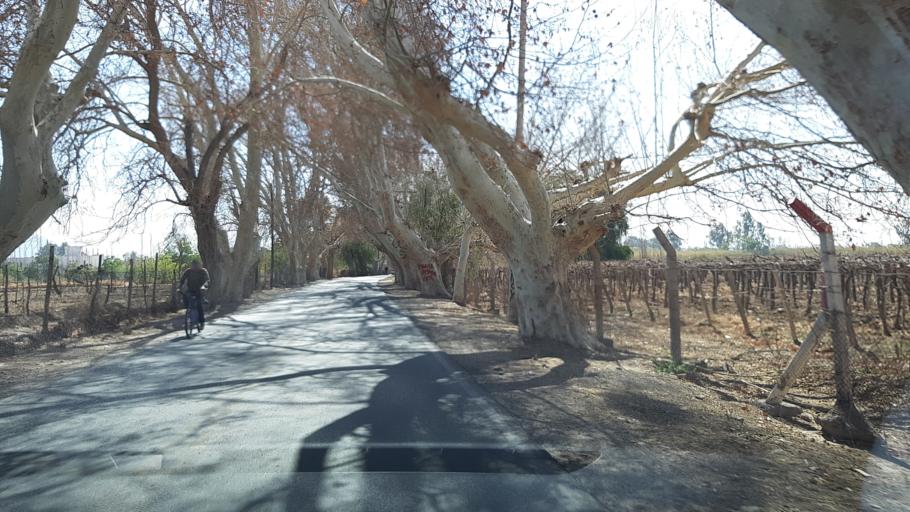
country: AR
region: San Juan
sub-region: Departamento de Rivadavia
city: Rivadavia
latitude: -31.5287
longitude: -68.6191
